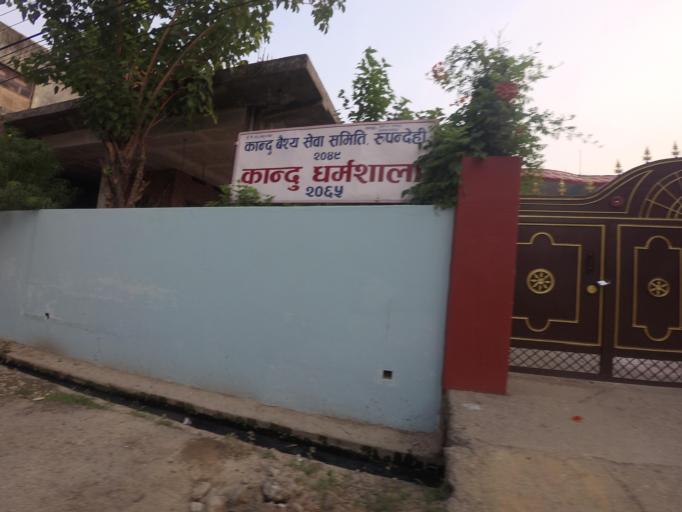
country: NP
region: Western Region
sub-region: Lumbini Zone
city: Bhairahawa
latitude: 27.5086
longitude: 83.4476
